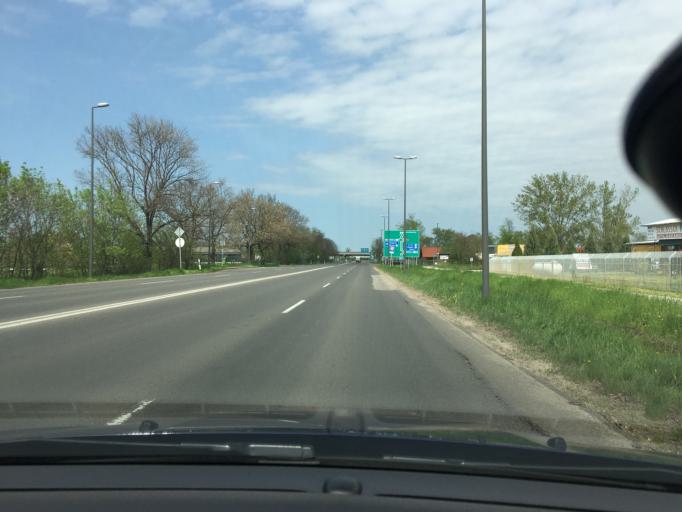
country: HU
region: Csongrad
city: Szeged
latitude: 46.2906
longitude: 20.1743
